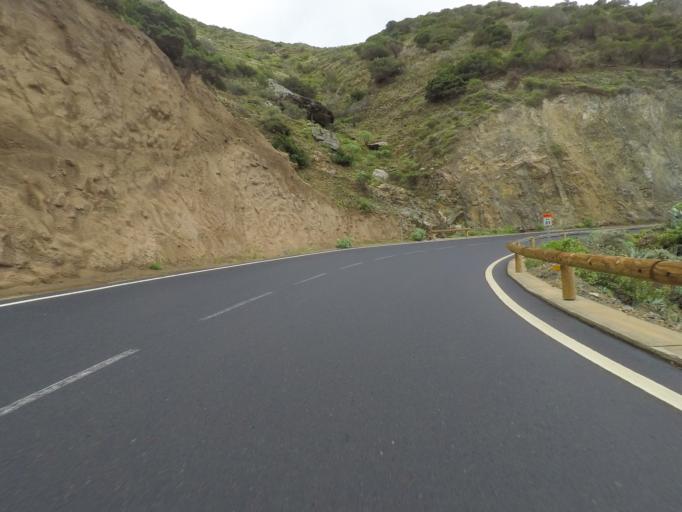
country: ES
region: Canary Islands
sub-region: Provincia de Santa Cruz de Tenerife
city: Vallehermosa
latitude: 28.1860
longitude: -17.2602
